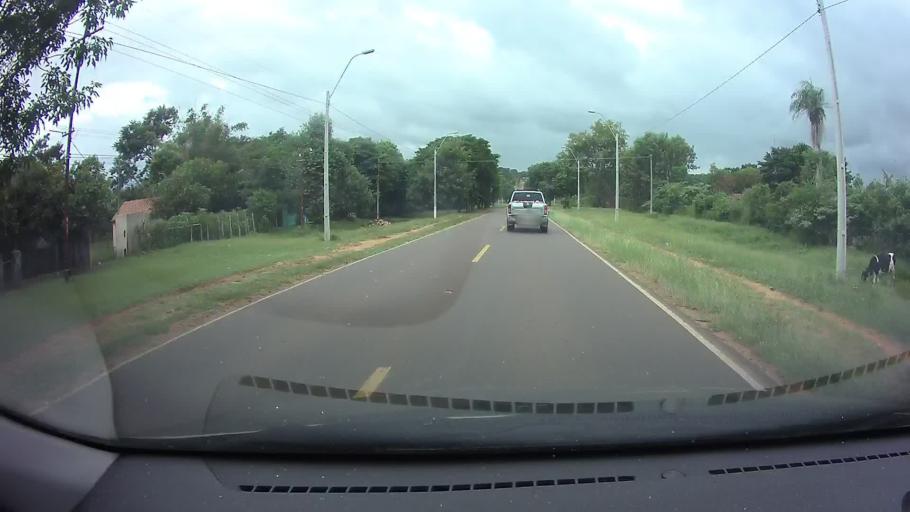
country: PY
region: Central
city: Nueva Italia
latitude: -25.6079
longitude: -57.4795
